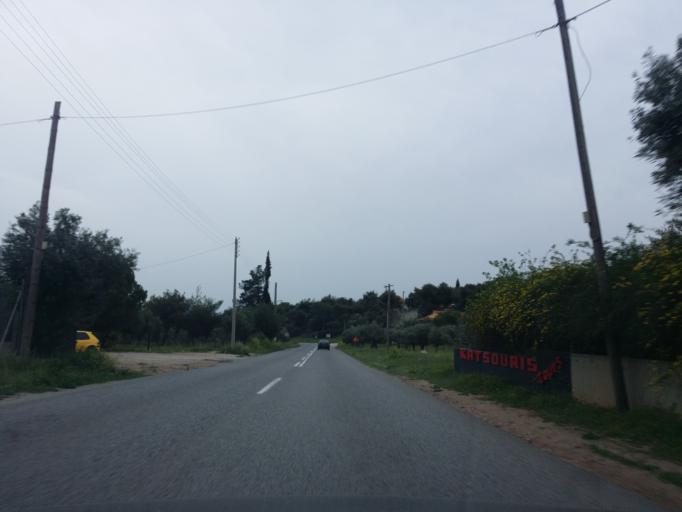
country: GR
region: Attica
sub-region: Nomarchia Dytikis Attikis
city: Mandra
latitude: 38.0867
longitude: 23.4831
